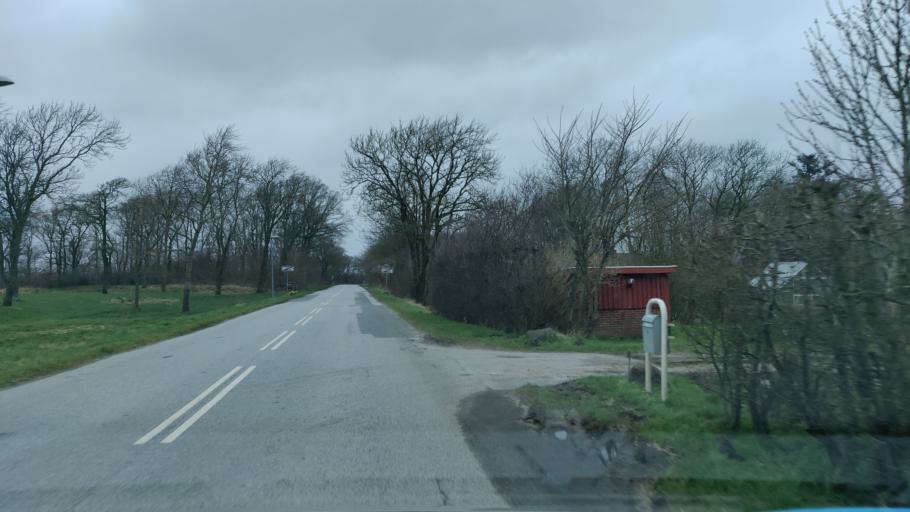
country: DK
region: Central Jutland
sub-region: Skive Kommune
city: Hojslev
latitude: 56.5557
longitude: 9.2477
